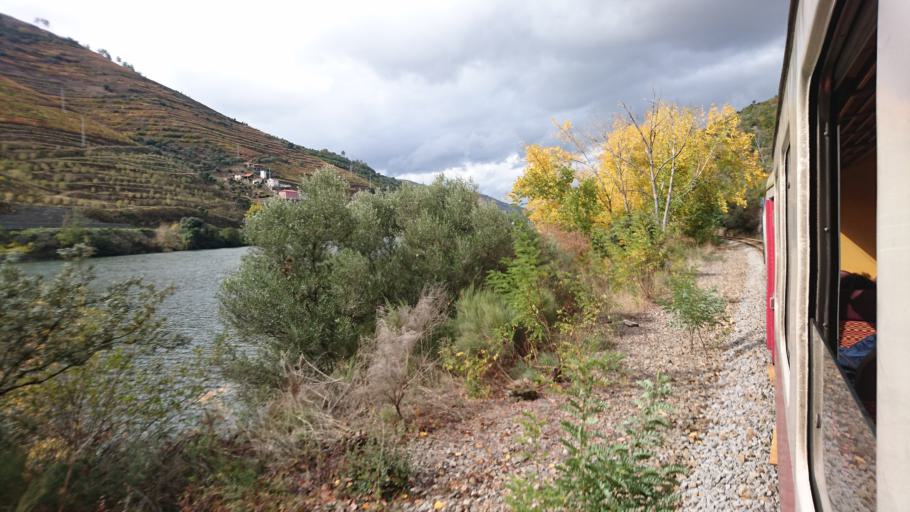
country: PT
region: Viseu
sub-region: Armamar
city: Armamar
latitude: 41.1439
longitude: -7.7054
